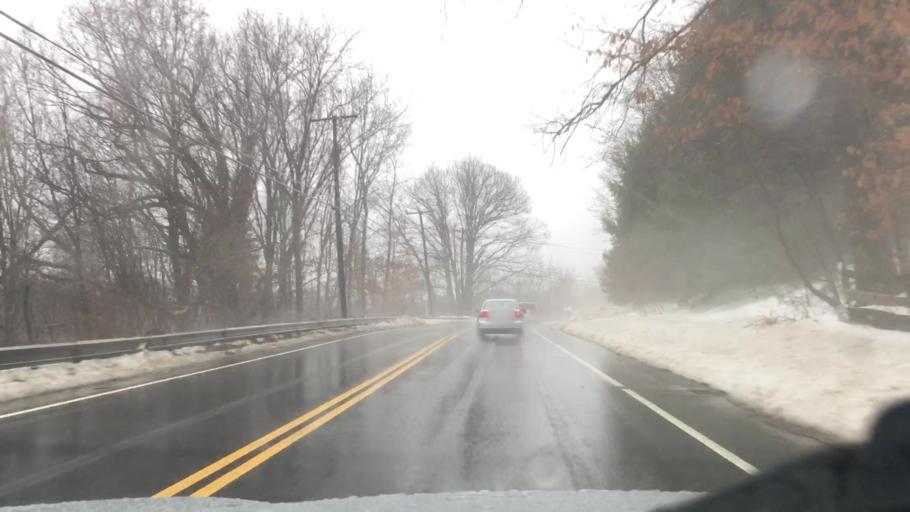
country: US
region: Massachusetts
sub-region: Hampden County
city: Ludlow
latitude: 42.1886
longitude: -72.5034
